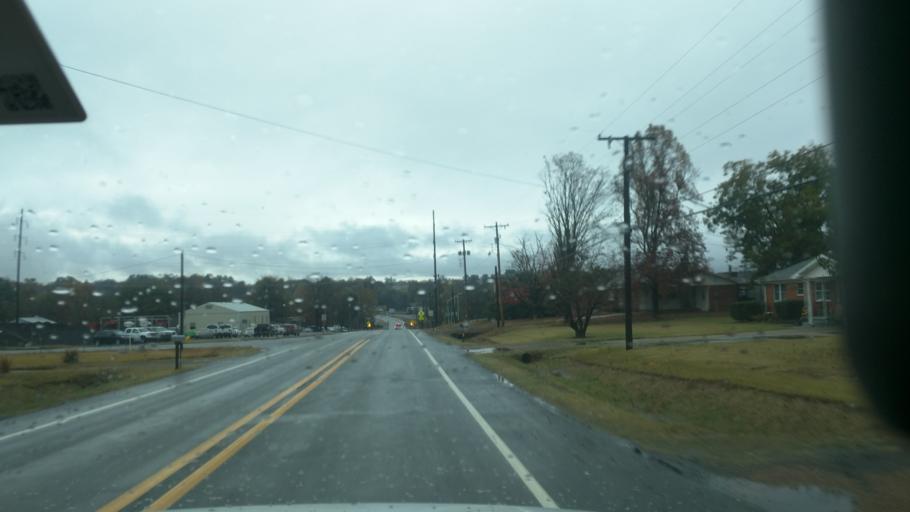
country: US
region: Arkansas
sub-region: Franklin County
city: Ozark
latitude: 35.4954
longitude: -93.8436
